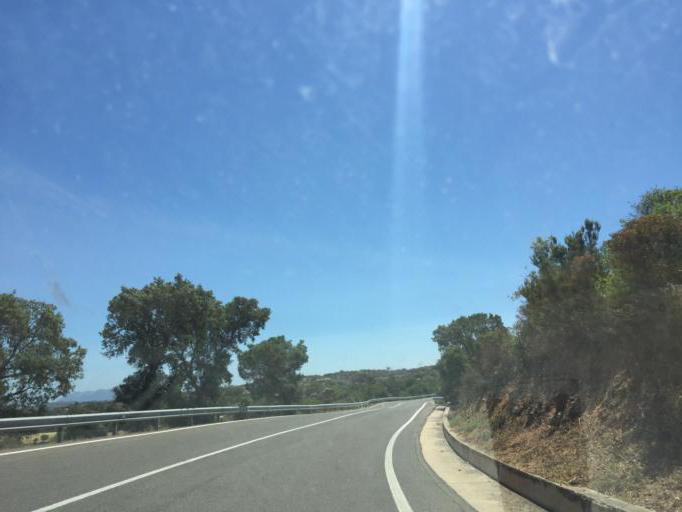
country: IT
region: Sardinia
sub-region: Provincia di Olbia-Tempio
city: Telti
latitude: 40.8914
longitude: 9.3247
